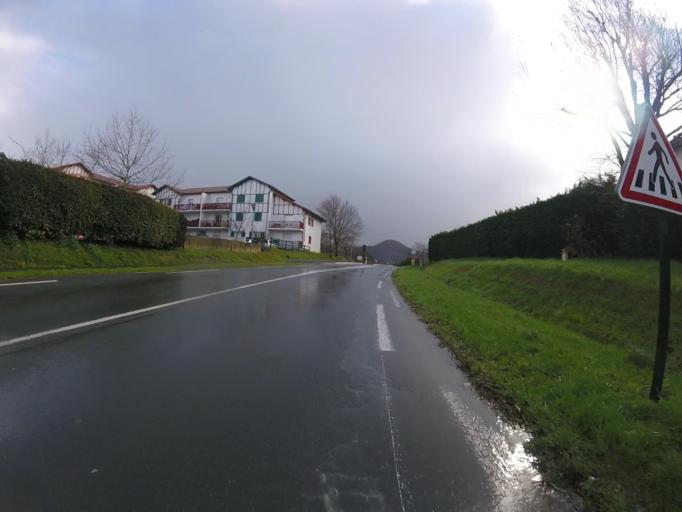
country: FR
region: Aquitaine
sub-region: Departement des Pyrenees-Atlantiques
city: Ascain
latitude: 43.3423
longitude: -1.6383
